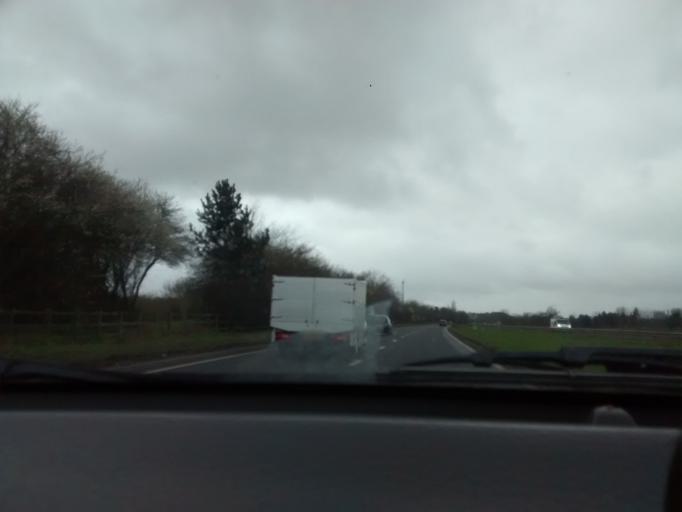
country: GB
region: England
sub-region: Suffolk
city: Felixstowe
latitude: 51.9811
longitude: 1.3268
